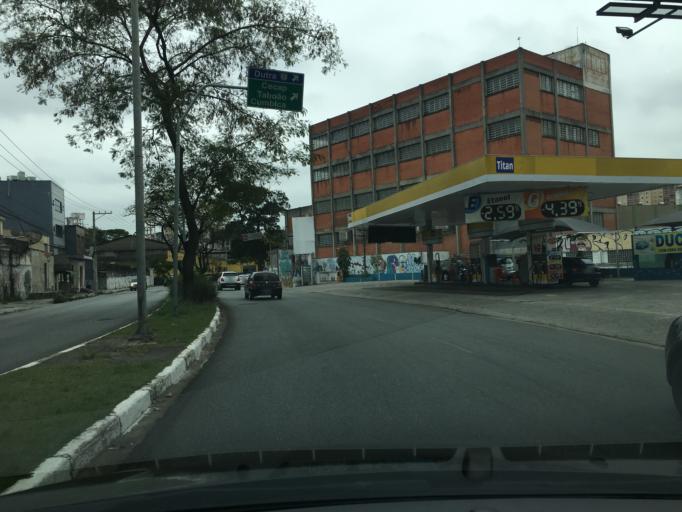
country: BR
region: Sao Paulo
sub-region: Guarulhos
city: Guarulhos
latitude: -23.4804
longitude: -46.5362
